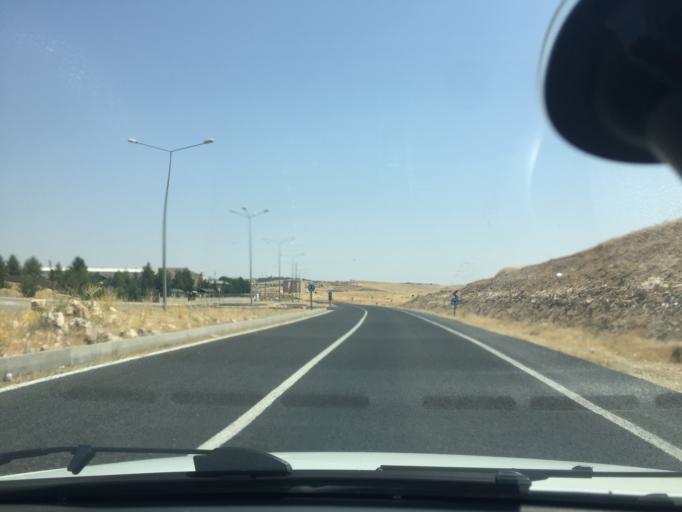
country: TR
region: Mardin
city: Acirli
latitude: 37.4392
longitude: 41.2953
